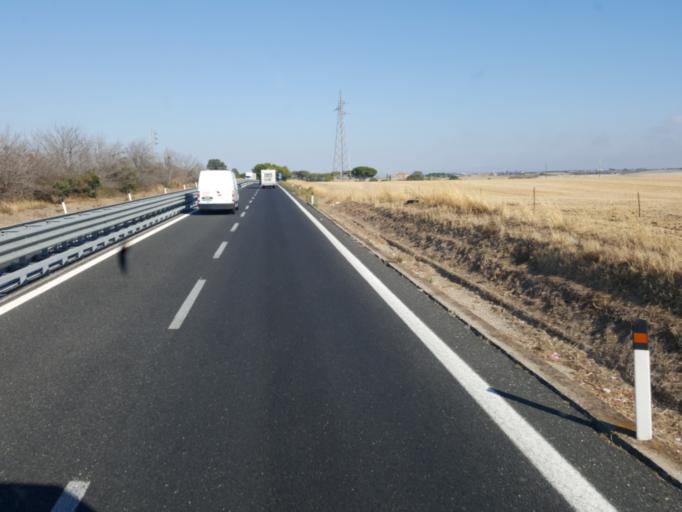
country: IT
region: Latium
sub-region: Provincia di Viterbo
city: Pescia Romana
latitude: 42.3919
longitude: 11.5362
